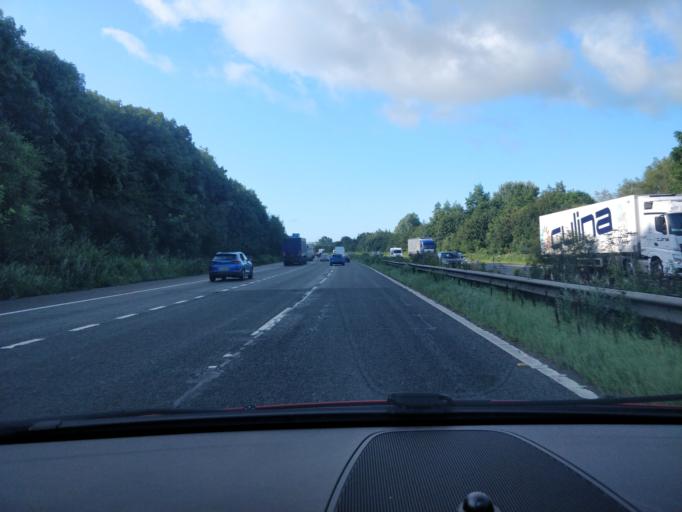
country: GB
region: England
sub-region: Knowsley
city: Prescot
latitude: 53.4112
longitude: -2.8136
